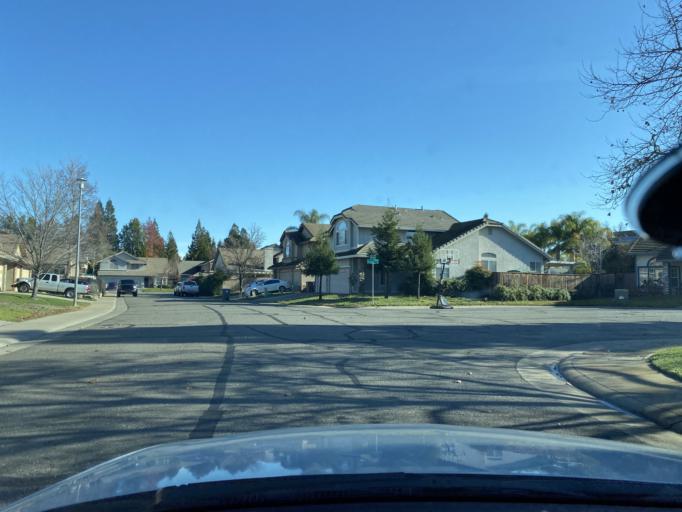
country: US
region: California
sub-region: Sacramento County
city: Elk Grove
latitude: 38.4327
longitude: -121.3827
